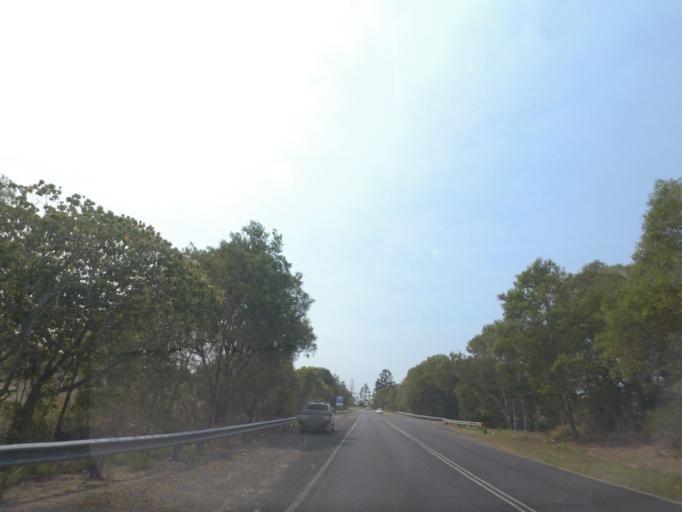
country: AU
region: New South Wales
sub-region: Byron Shire
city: Brunswick Heads
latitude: -28.4947
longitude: 153.5261
